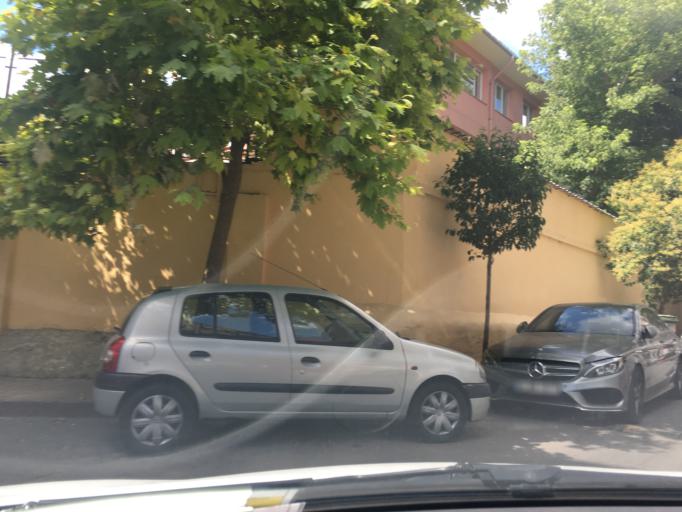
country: TR
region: Istanbul
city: Istanbul
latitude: 41.0117
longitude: 28.9369
